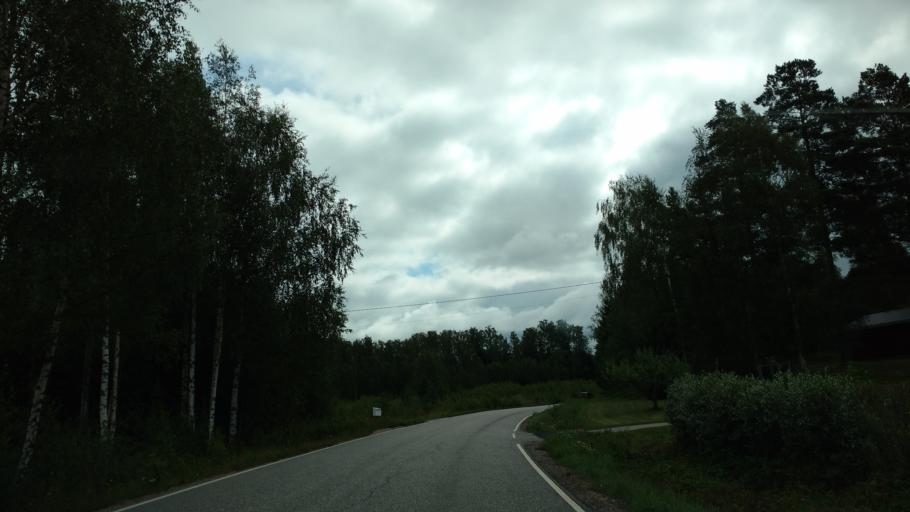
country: FI
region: Varsinais-Suomi
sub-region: Aboland-Turunmaa
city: Dragsfjaerd
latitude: 60.0317
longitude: 22.4444
